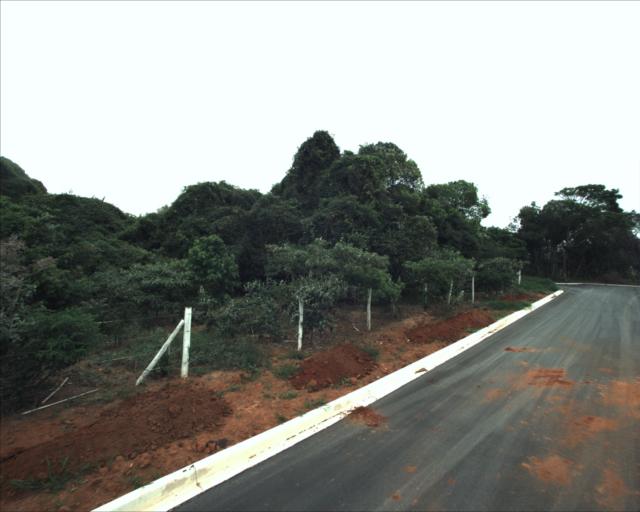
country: BR
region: Sao Paulo
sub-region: Sorocaba
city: Sorocaba
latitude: -23.4208
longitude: -47.4276
